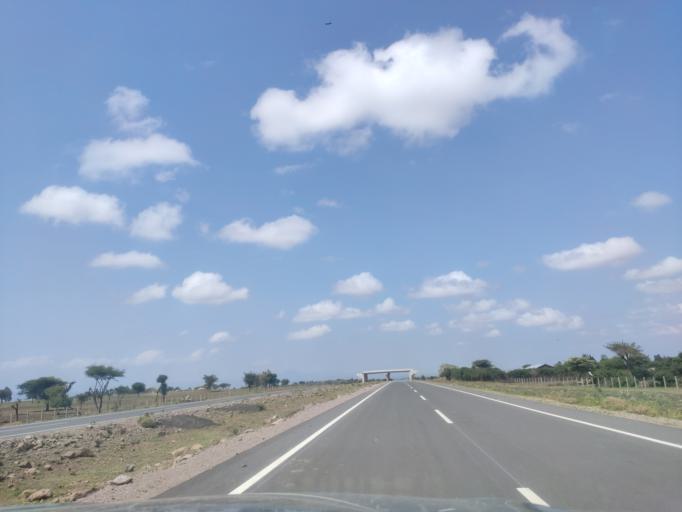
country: ET
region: Oromiya
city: Mojo
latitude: 8.5393
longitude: 39.0994
